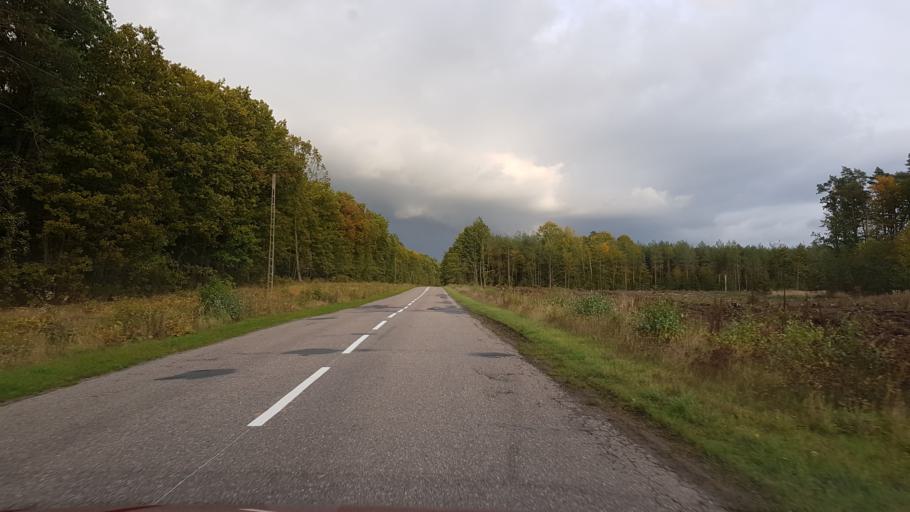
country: PL
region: West Pomeranian Voivodeship
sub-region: Powiat walecki
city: Tuczno
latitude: 53.1746
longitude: 16.3254
